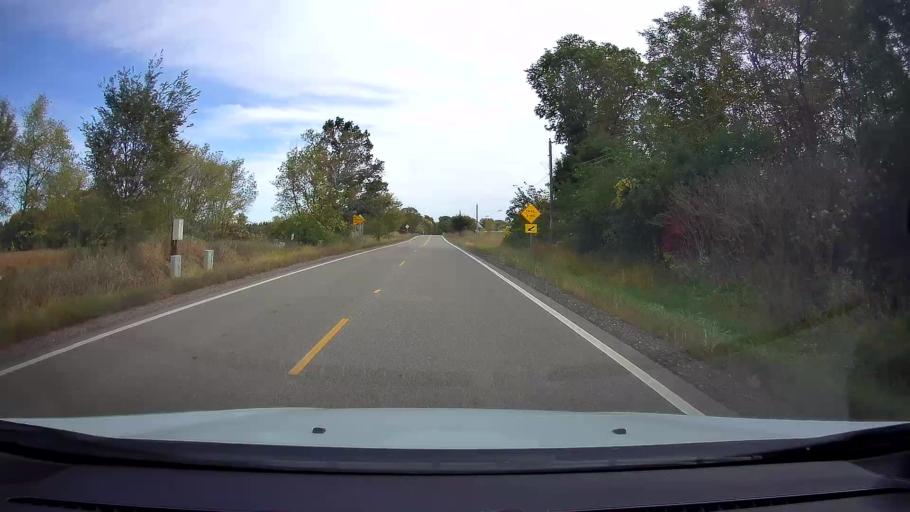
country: US
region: Minnesota
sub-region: Washington County
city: Stillwater
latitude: 45.0970
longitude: -92.8184
